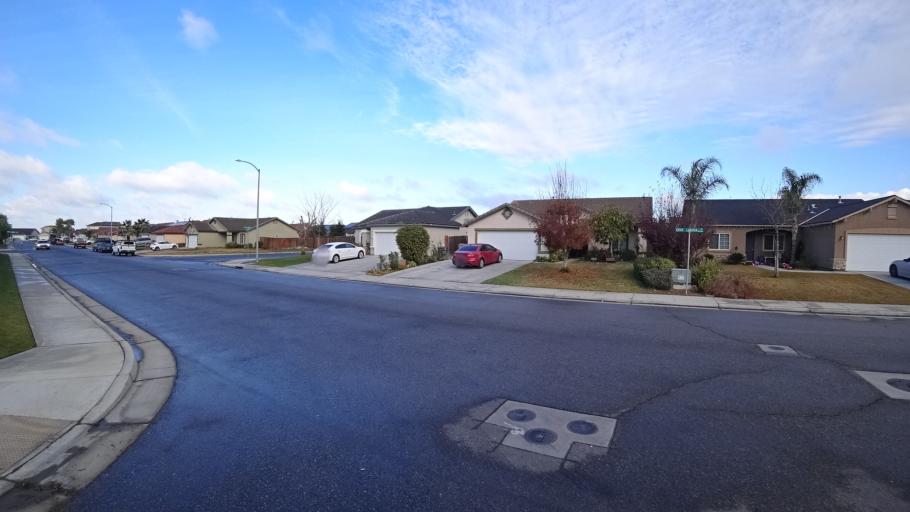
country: US
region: California
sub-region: Kern County
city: Greenfield
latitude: 35.2898
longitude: -118.9954
